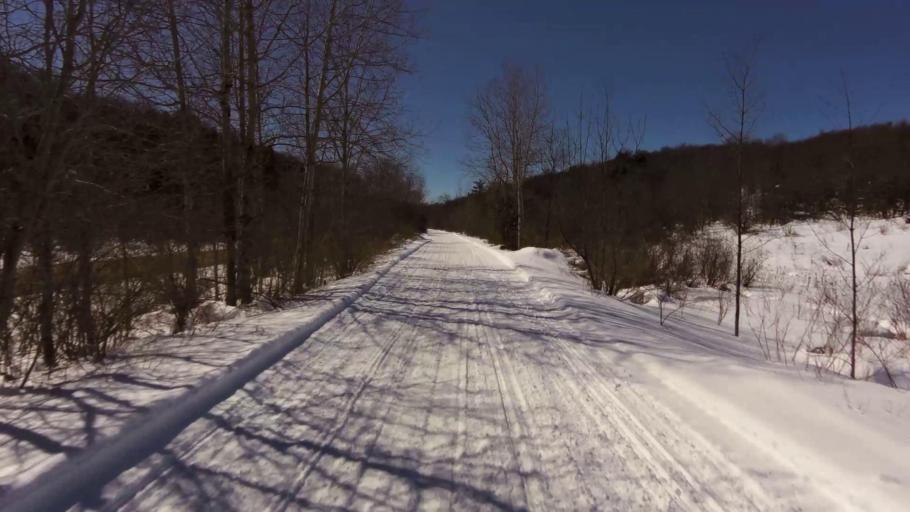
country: US
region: New York
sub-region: Cattaraugus County
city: Delevan
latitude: 42.4378
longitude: -78.4360
